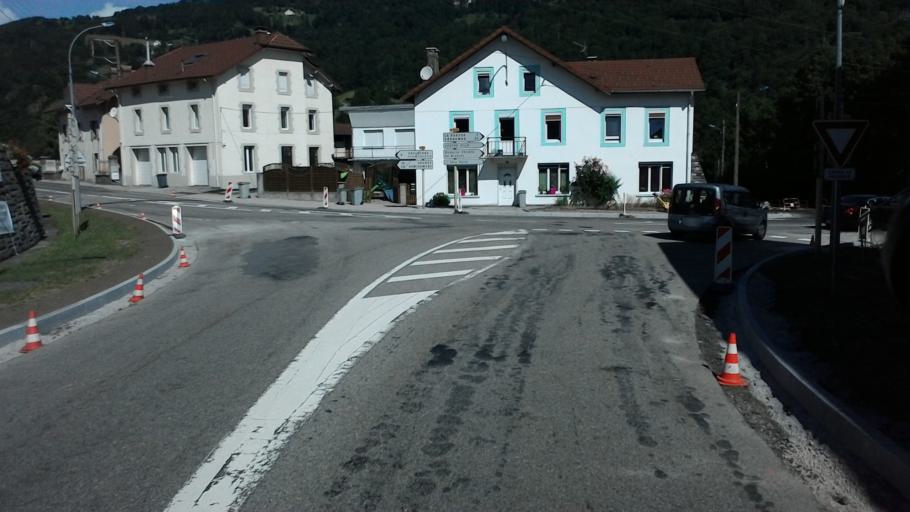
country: FR
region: Lorraine
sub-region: Departement des Vosges
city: Cornimont
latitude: 47.9541
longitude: 6.8243
